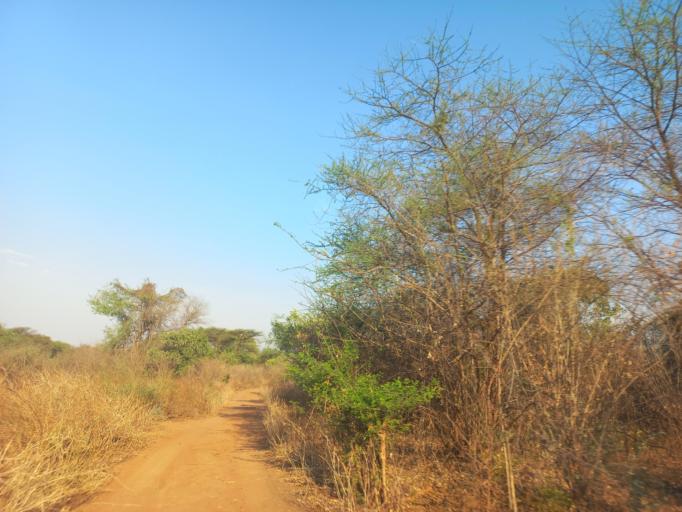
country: ZM
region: Lusaka
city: Luangwa
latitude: -15.4207
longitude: 30.2698
